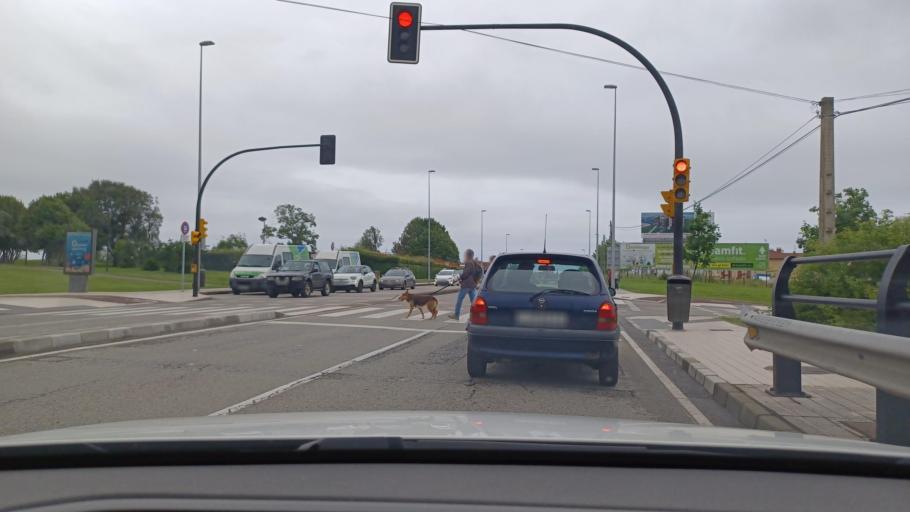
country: ES
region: Asturias
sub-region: Province of Asturias
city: Gijon
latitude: 43.5275
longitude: -5.6550
